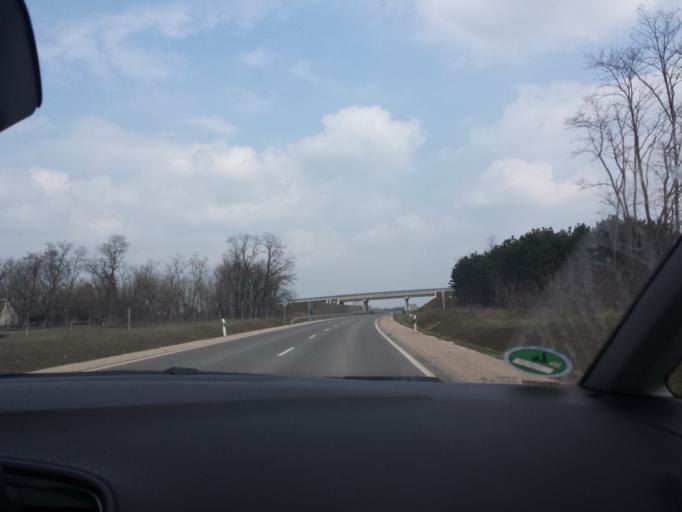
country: HU
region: Bacs-Kiskun
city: Kecskemet
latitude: 46.9476
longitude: 19.6686
